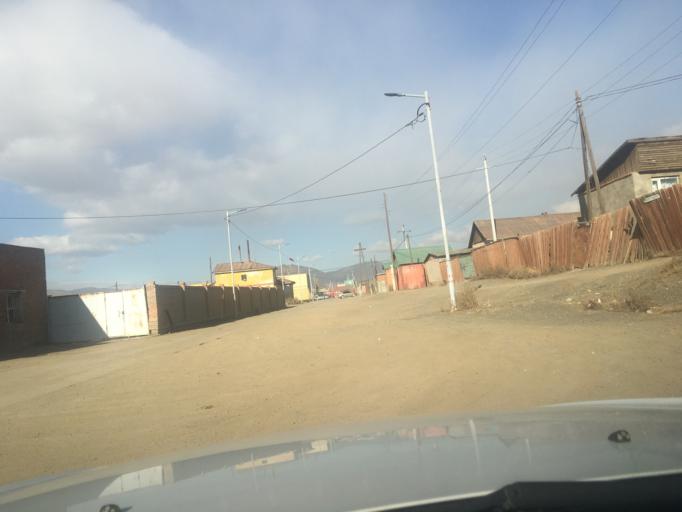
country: MN
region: Ulaanbaatar
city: Ulaanbaatar
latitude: 47.9442
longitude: 106.8254
